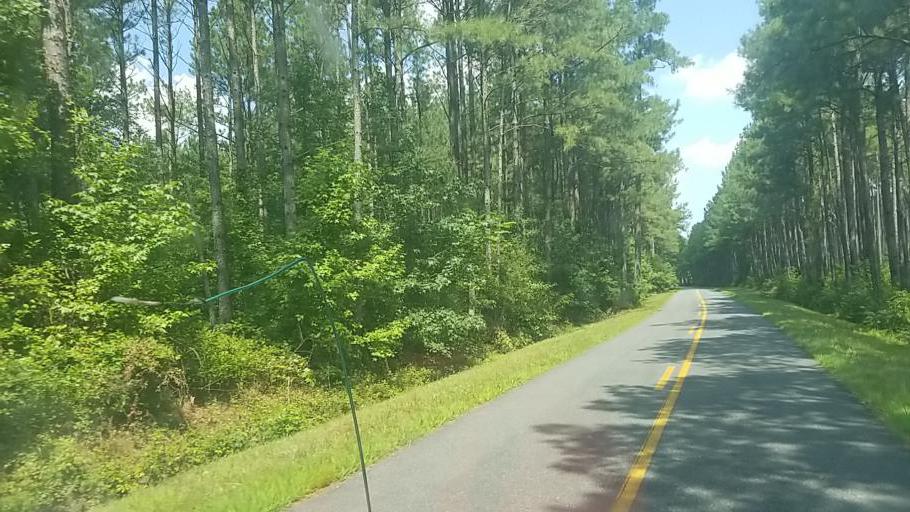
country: US
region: Maryland
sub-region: Worcester County
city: Snow Hill
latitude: 38.2717
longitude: -75.4716
